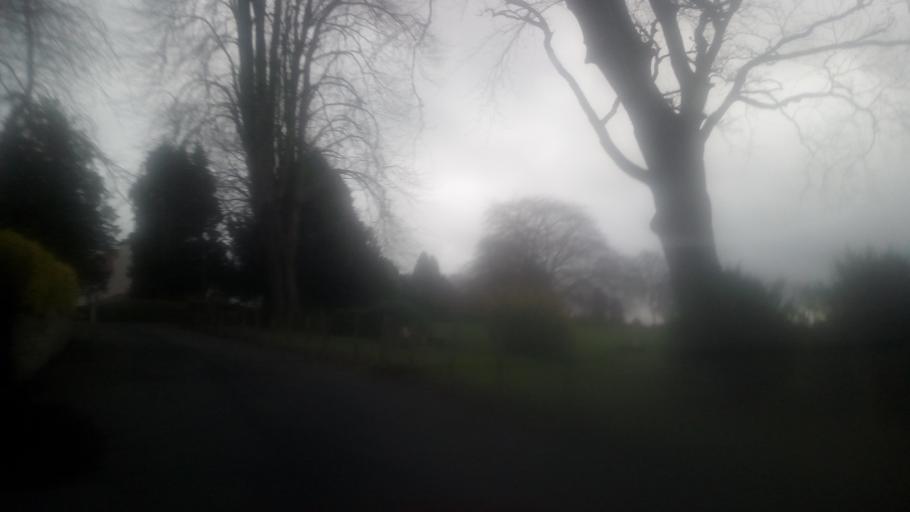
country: GB
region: Scotland
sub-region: The Scottish Borders
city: Jedburgh
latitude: 55.4742
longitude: -2.5512
